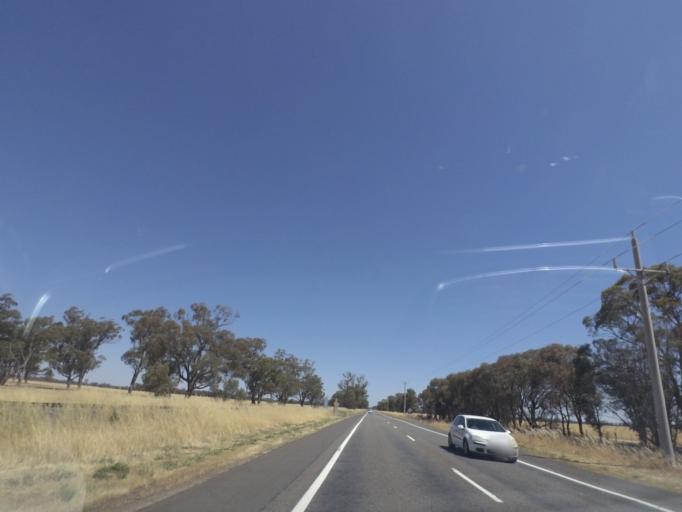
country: AU
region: Victoria
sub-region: Greater Shepparton
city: Shepparton
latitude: -36.2006
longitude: 145.4318
